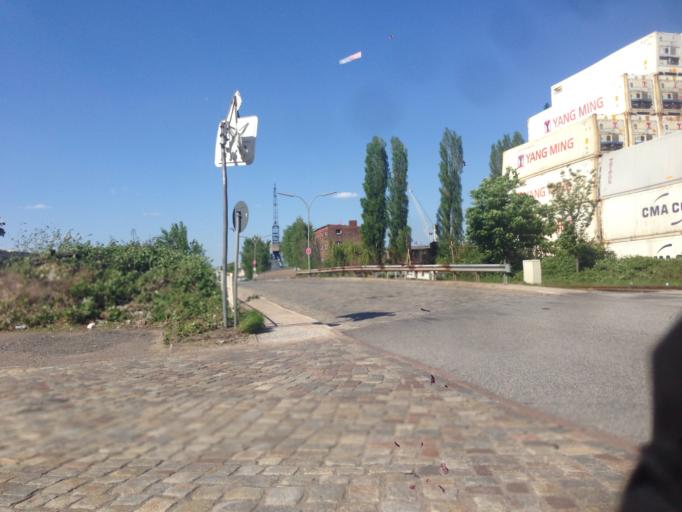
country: DE
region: Hamburg
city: Kleiner Grasbrook
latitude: 53.5324
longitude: 9.9730
